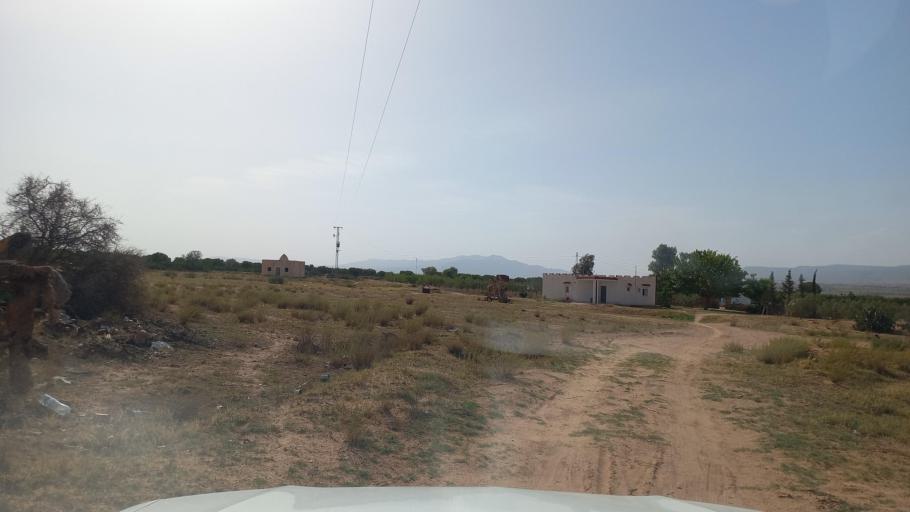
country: TN
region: Al Qasrayn
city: Kasserine
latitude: 35.2053
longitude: 8.9697
